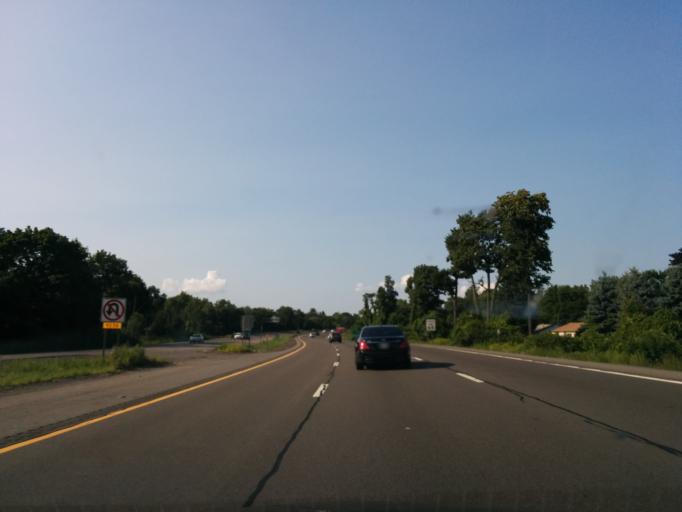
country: US
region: New York
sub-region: Onondaga County
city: North Syracuse
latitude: 43.1305
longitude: -76.1195
